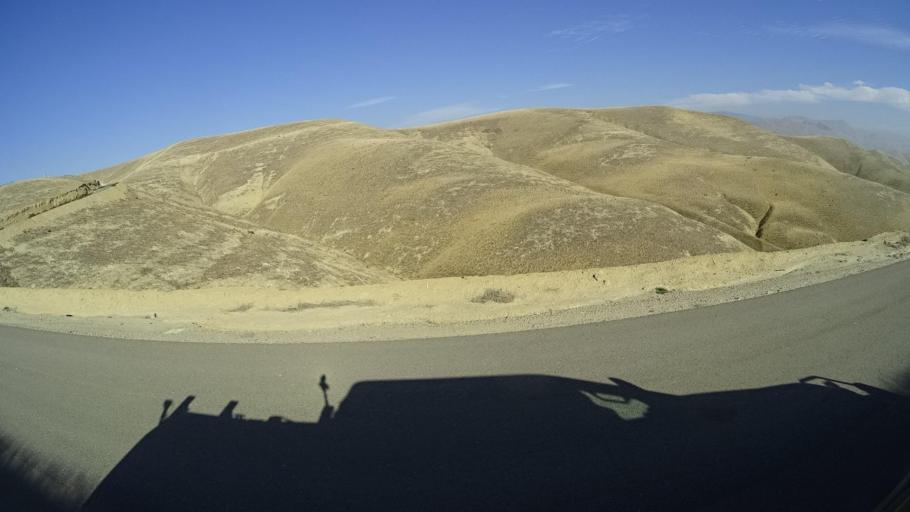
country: US
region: California
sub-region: Kern County
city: Oildale
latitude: 35.4657
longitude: -118.8714
